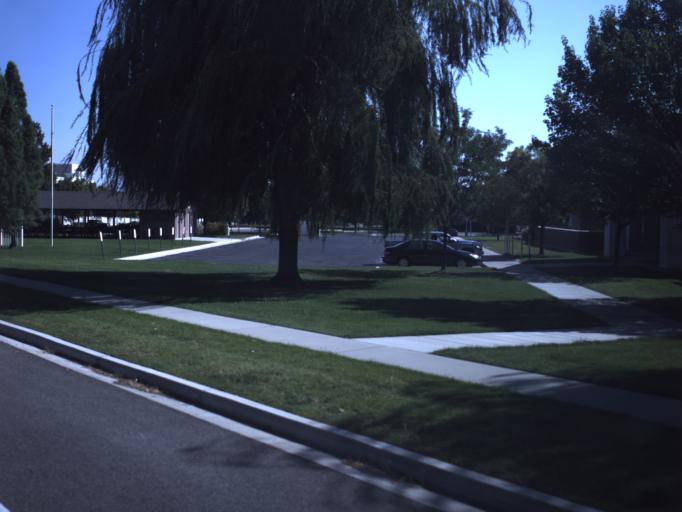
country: US
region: Utah
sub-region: Utah County
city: Cedar Hills
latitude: 40.3956
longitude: -111.7722
